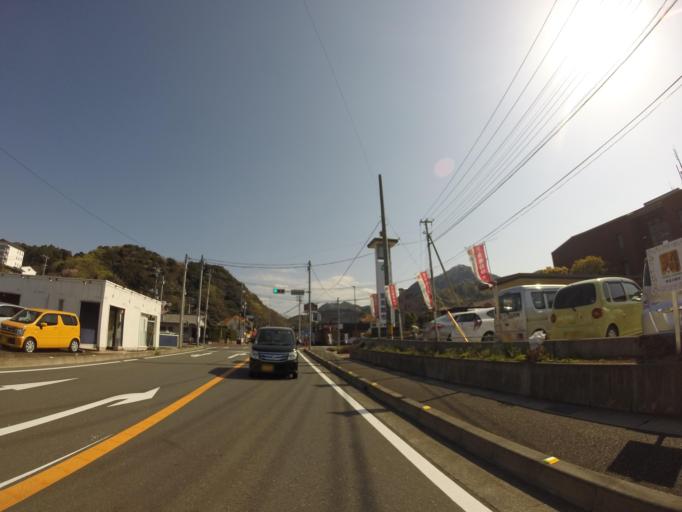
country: JP
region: Shizuoka
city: Mishima
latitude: 35.0280
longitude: 138.9296
